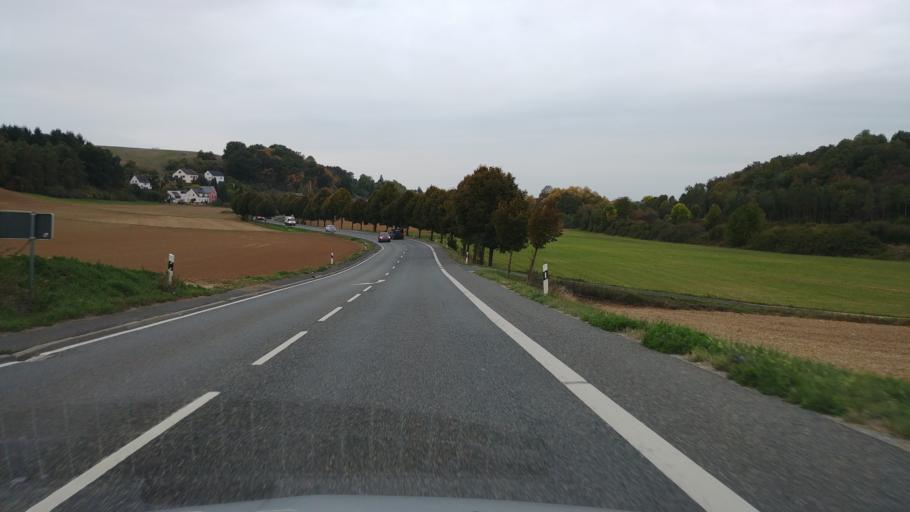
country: DE
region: Rheinland-Pfalz
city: Niederneisen
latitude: 50.3266
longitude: 8.0641
